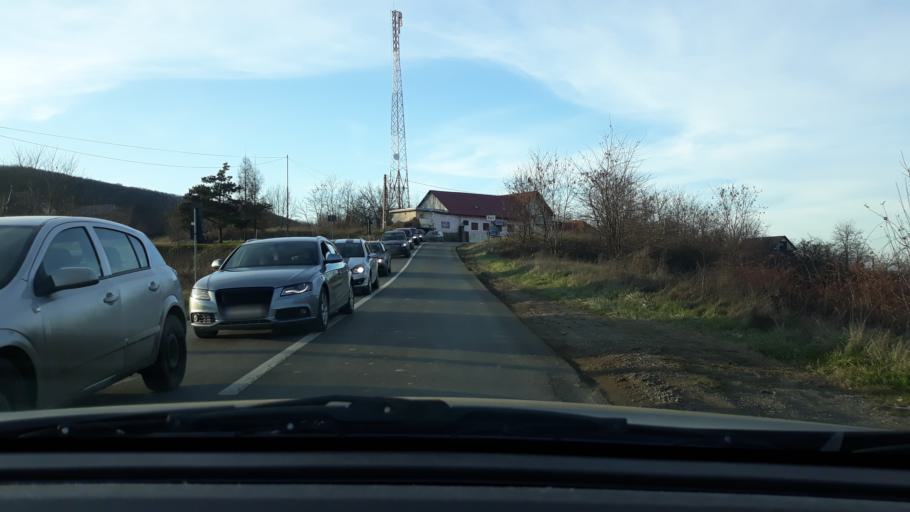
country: RO
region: Salaj
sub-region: Comuna Marca
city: Marca
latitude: 47.2265
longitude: 22.5539
